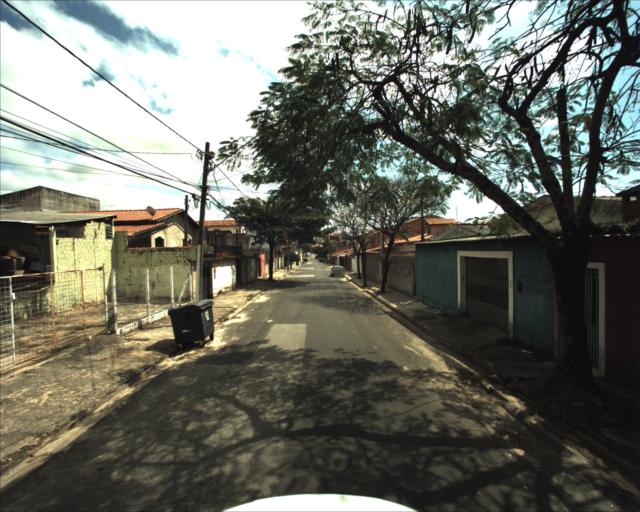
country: BR
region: Sao Paulo
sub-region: Sorocaba
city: Sorocaba
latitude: -23.4947
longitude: -47.4805
